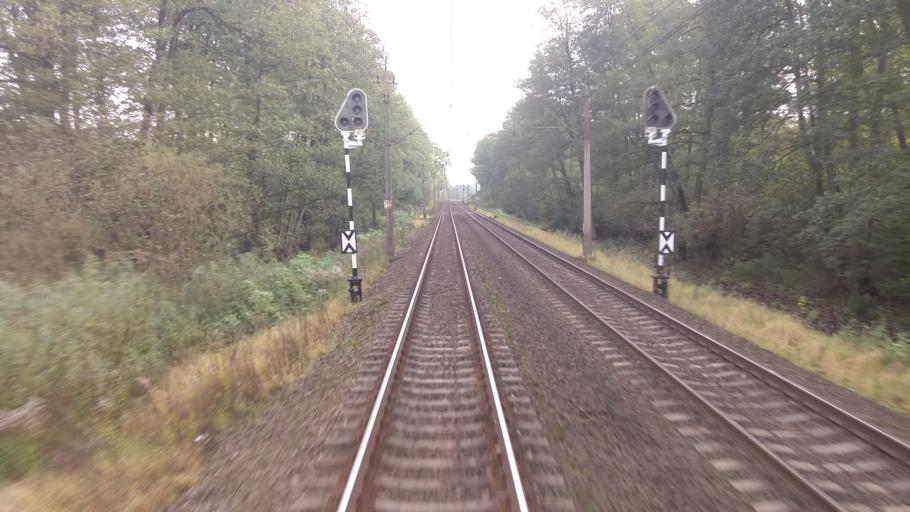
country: PL
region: West Pomeranian Voivodeship
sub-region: Powiat stargardzki
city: Dolice
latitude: 53.1837
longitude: 15.2663
